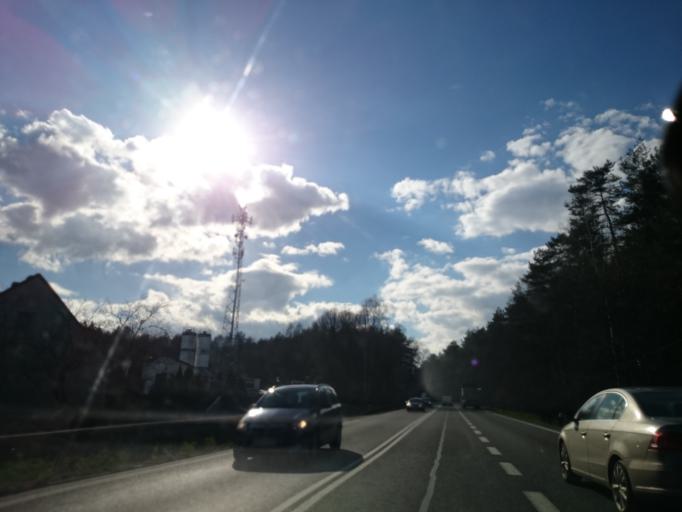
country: PL
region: Opole Voivodeship
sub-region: Powiat opolski
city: Dabrowa
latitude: 50.6879
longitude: 17.7389
